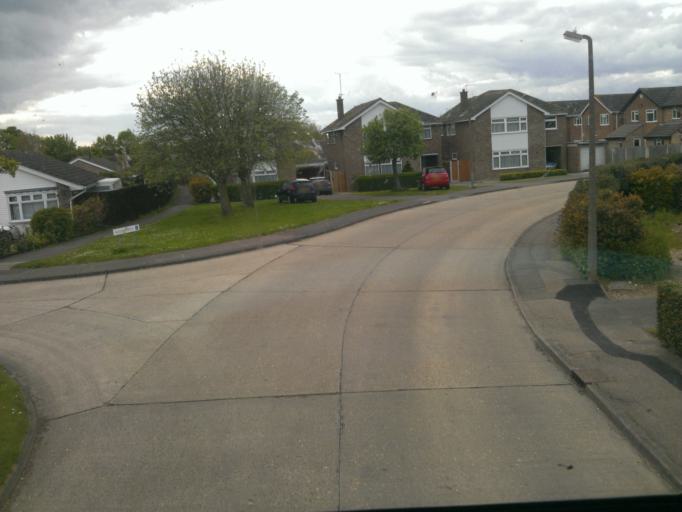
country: GB
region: England
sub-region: Essex
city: Marks Tey
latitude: 51.8761
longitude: 0.7649
